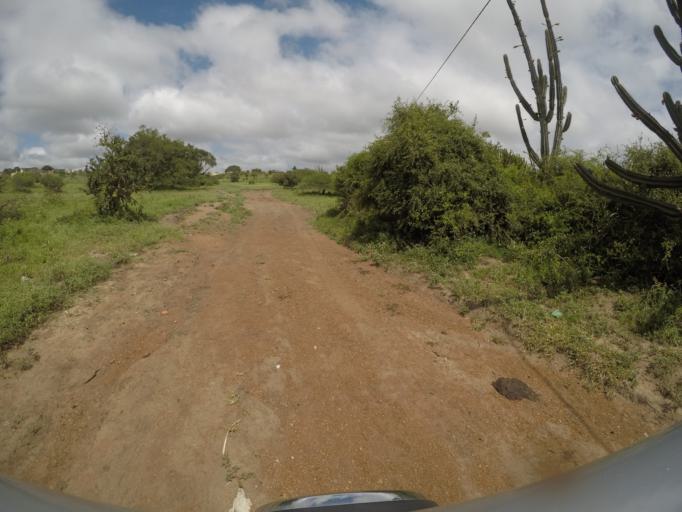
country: ZA
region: KwaZulu-Natal
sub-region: uThungulu District Municipality
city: Empangeni
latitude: -28.5721
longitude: 31.8426
